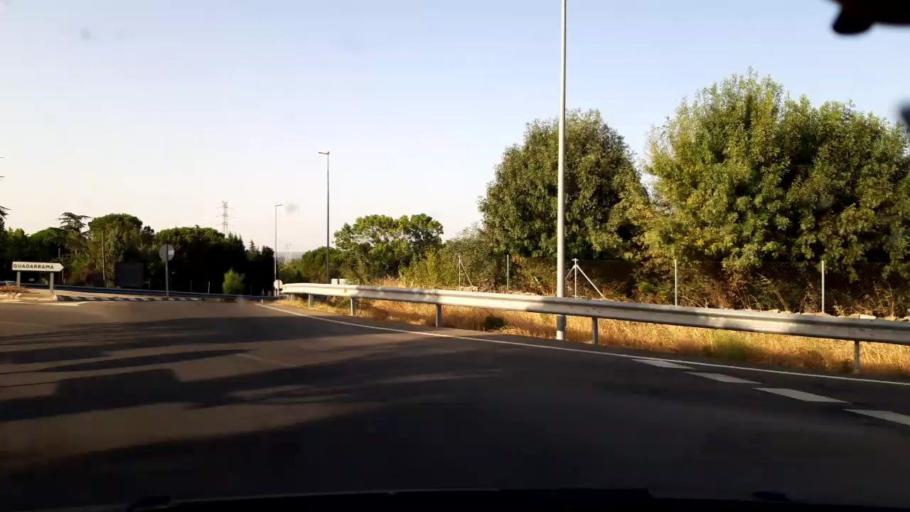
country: ES
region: Madrid
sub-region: Provincia de Madrid
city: Collado Mediano
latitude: 40.6923
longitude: -4.0479
